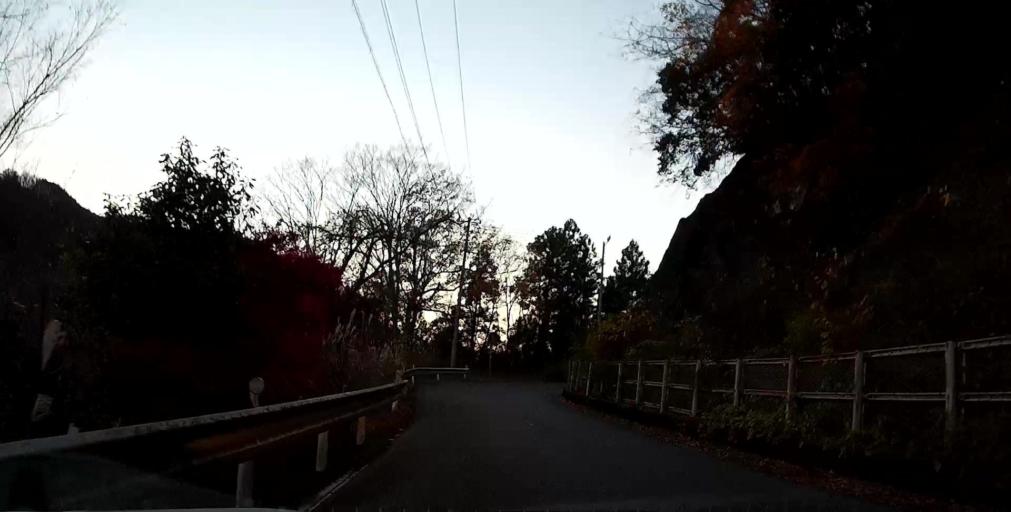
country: JP
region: Yamanashi
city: Uenohara
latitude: 35.5726
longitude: 139.1960
